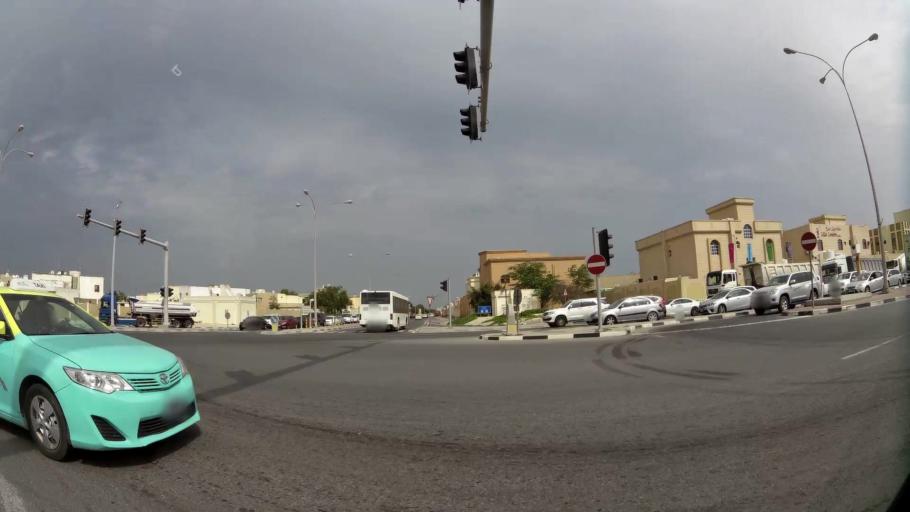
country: QA
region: Baladiyat ad Dawhah
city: Doha
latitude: 25.3422
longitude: 51.5057
